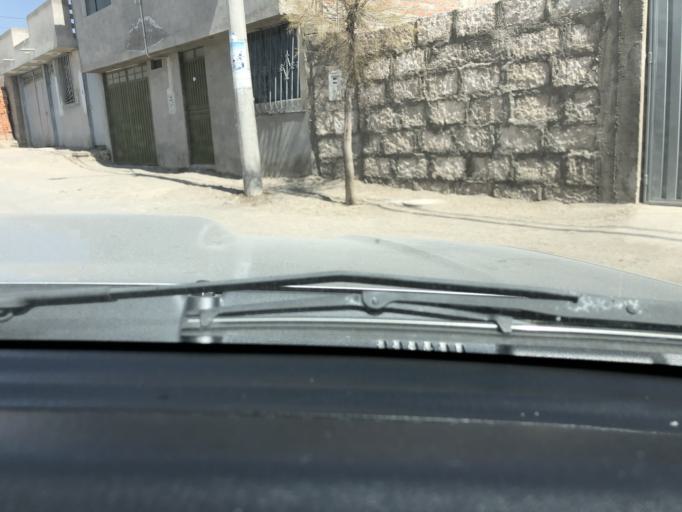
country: PE
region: Arequipa
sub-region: Provincia de Arequipa
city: Arequipa
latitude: -16.3419
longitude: -71.5511
